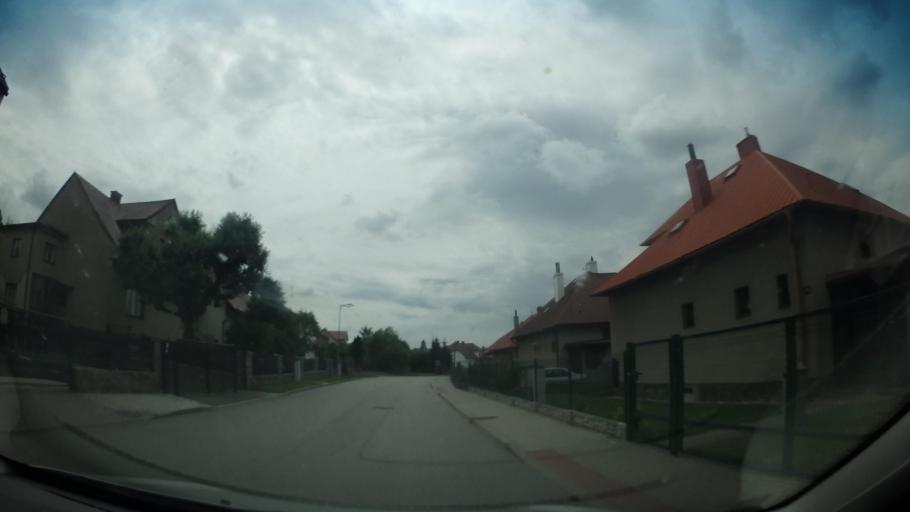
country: CZ
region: Vysocina
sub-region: Okres Zd'ar nad Sazavou
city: Nove Mesto na Morave
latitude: 49.5782
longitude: 16.0790
